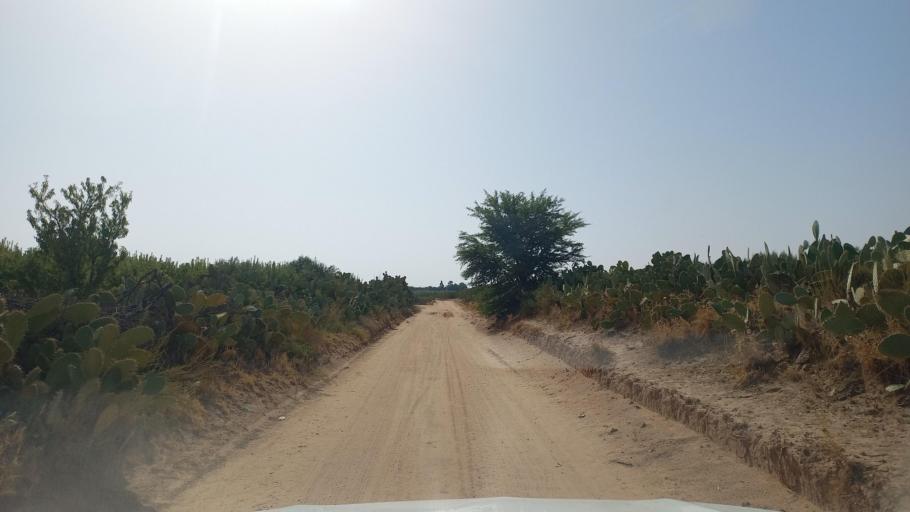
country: TN
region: Al Qasrayn
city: Kasserine
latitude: 35.2484
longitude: 9.0348
